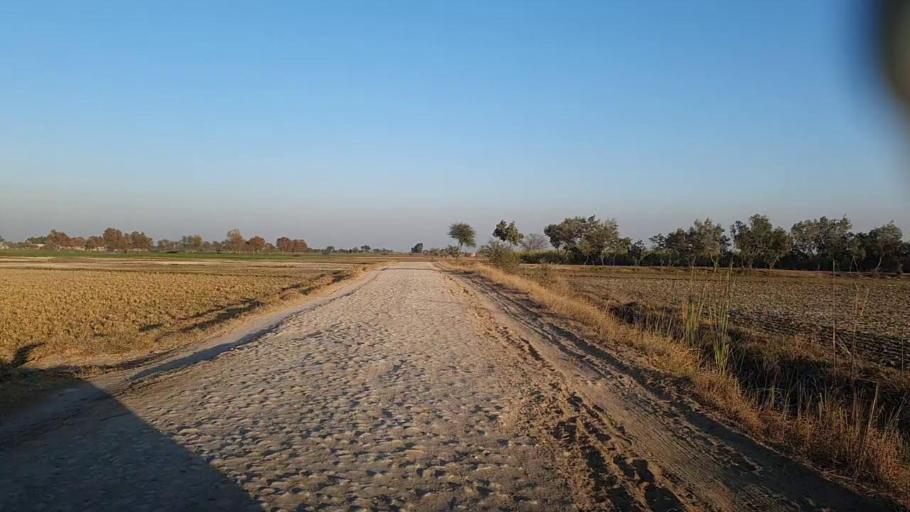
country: PK
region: Sindh
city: Khairpur
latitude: 27.9156
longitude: 69.6883
